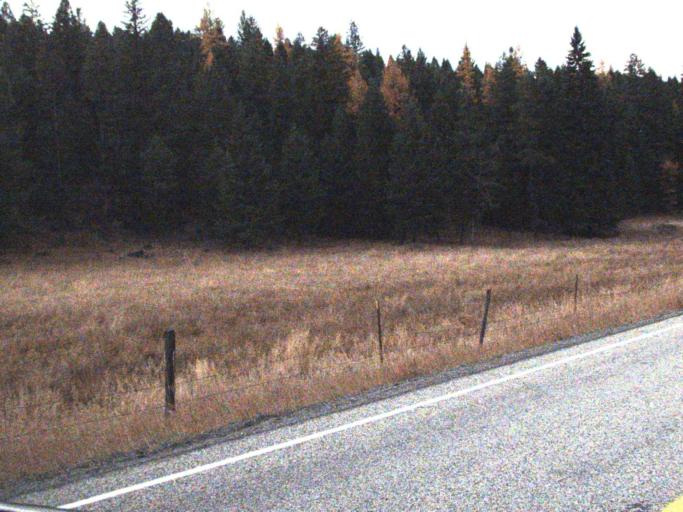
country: US
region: Washington
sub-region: Ferry County
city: Republic
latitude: 48.6065
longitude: -118.6583
